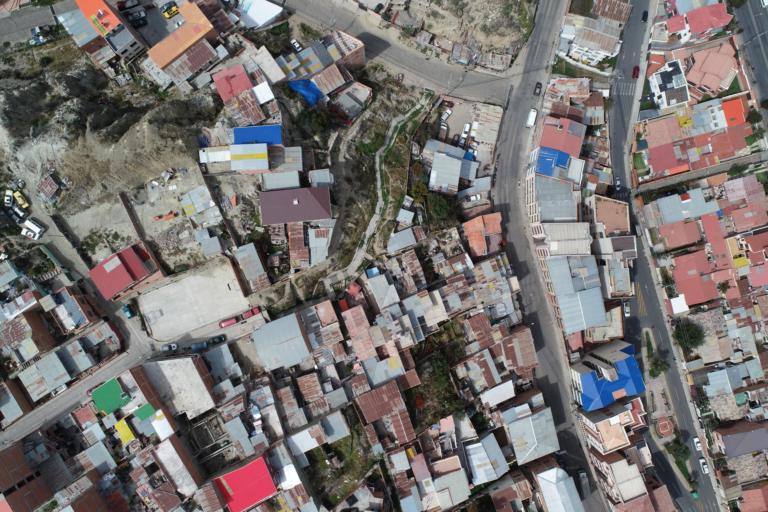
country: BO
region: La Paz
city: La Paz
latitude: -16.5332
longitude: -68.0962
